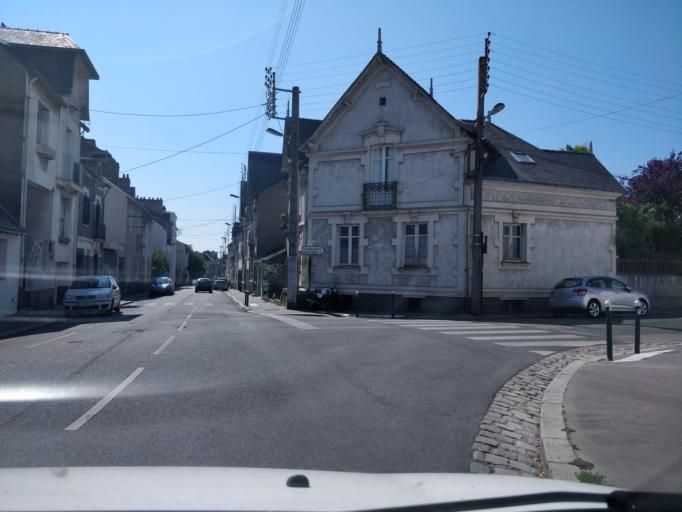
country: FR
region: Pays de la Loire
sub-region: Departement de la Loire-Atlantique
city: Nantes
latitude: 47.2257
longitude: -1.5405
